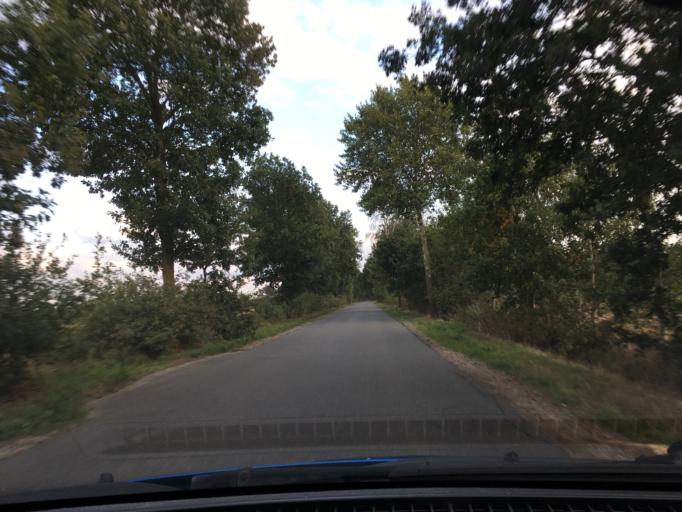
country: DE
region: Lower Saxony
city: Vierhofen
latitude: 53.2779
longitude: 10.1975
